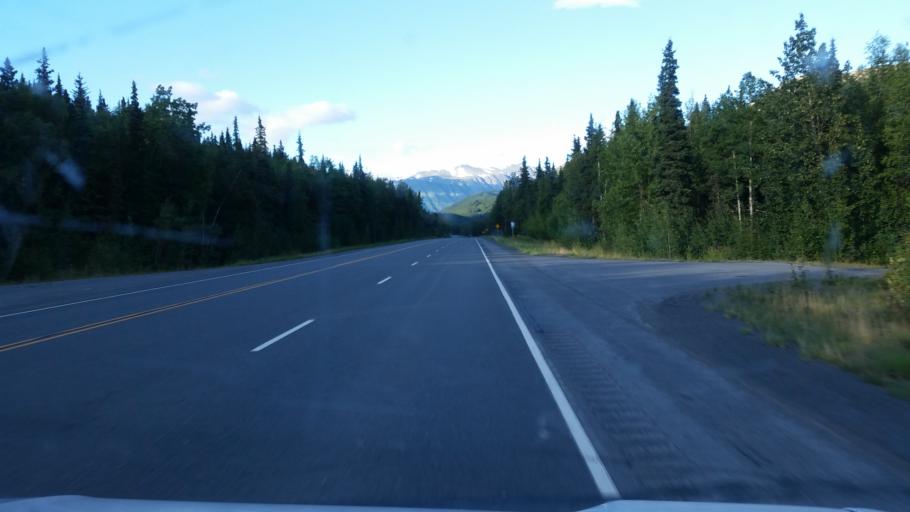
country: US
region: Alaska
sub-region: Kenai Peninsula Borough
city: Bear Creek
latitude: 60.4880
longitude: -149.7220
